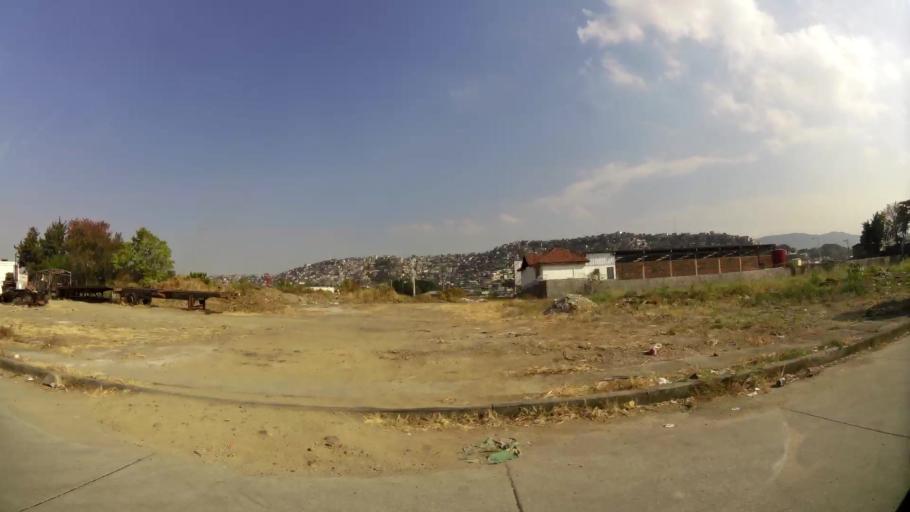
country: EC
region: Guayas
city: Guayaquil
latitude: -2.1393
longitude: -79.9259
